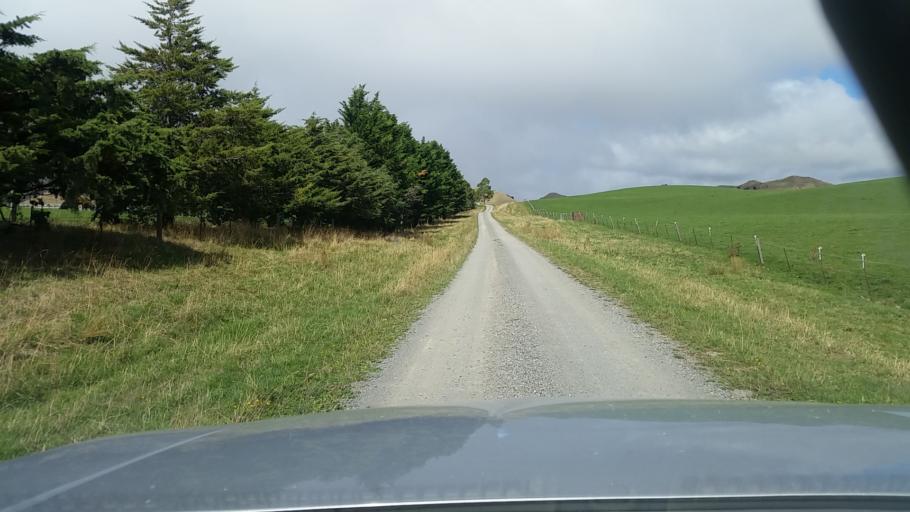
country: NZ
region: Marlborough
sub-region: Marlborough District
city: Blenheim
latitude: -41.7498
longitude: 173.8963
